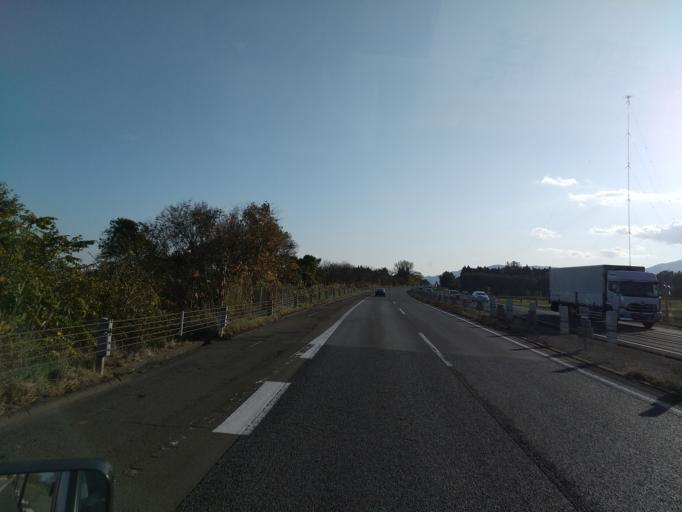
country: JP
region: Iwate
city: Morioka-shi
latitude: 39.6145
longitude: 141.1298
